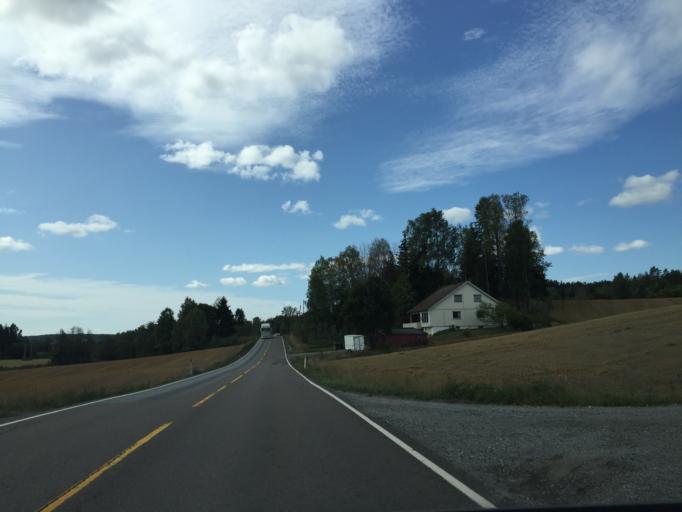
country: NO
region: Ostfold
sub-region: Hobol
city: Elvestad
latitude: 59.6096
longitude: 10.9234
